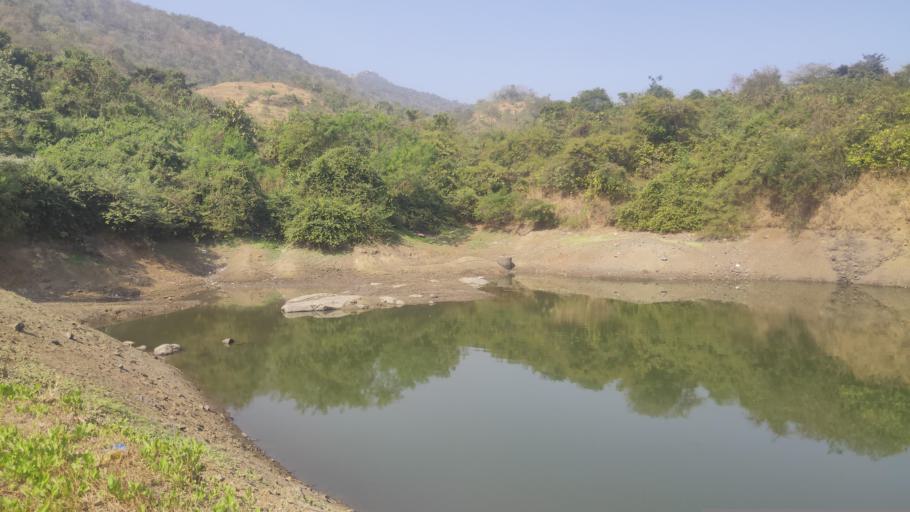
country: IN
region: Maharashtra
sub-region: Thane
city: Bhiwandi
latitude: 19.2926
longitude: 73.1057
